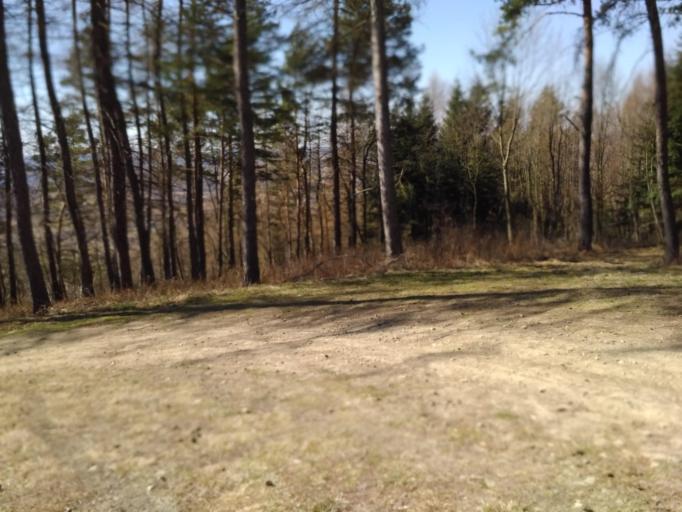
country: PL
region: Subcarpathian Voivodeship
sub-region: Powiat brzozowski
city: Blizne
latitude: 49.7553
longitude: 21.9913
